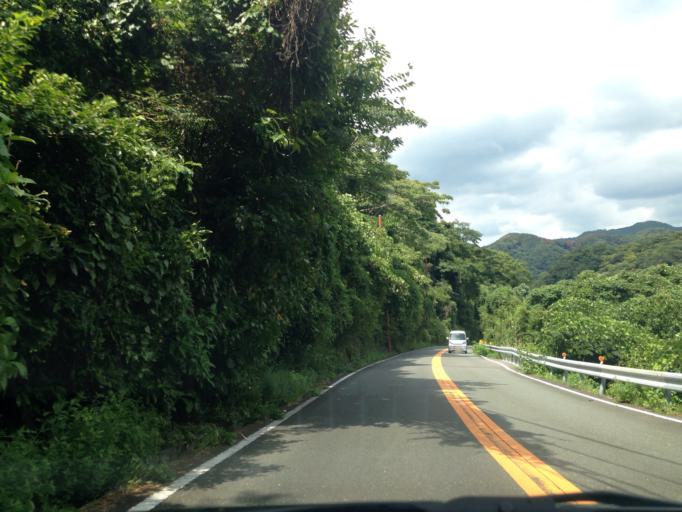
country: JP
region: Shizuoka
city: Shimoda
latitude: 34.6537
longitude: 138.7922
